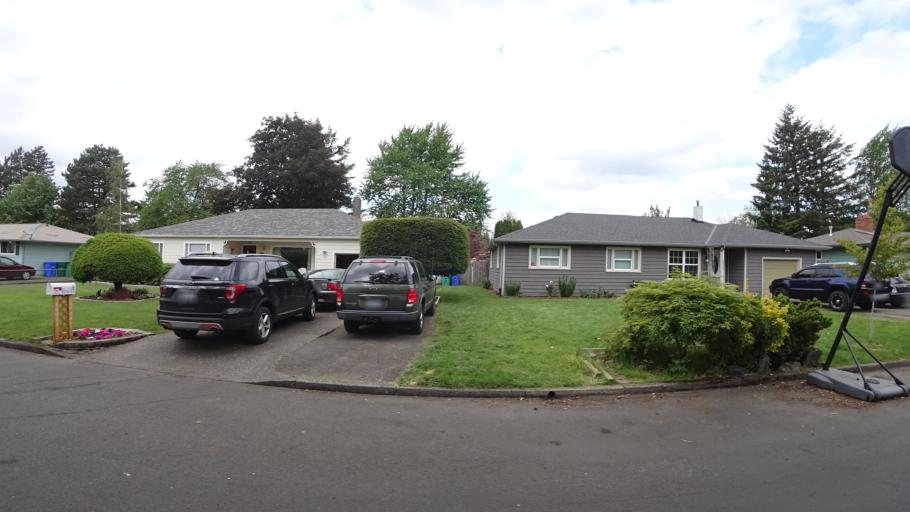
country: US
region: Oregon
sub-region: Multnomah County
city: Gresham
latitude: 45.5105
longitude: -122.4890
